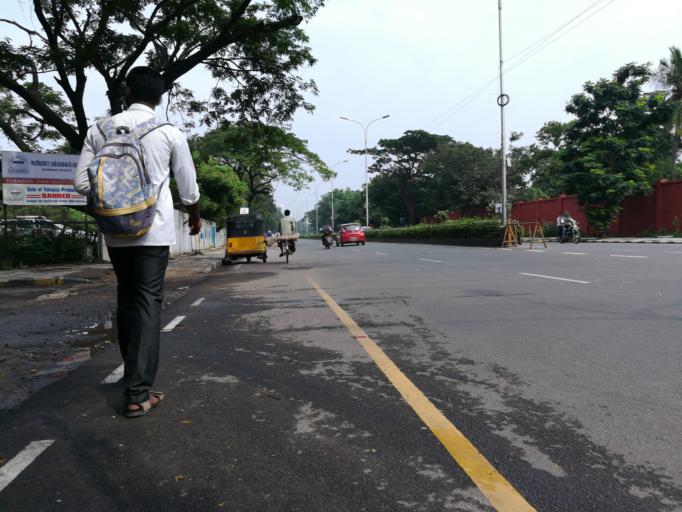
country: IN
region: Tamil Nadu
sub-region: Chennai
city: Gandhi Nagar
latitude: 13.0121
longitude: 80.2403
